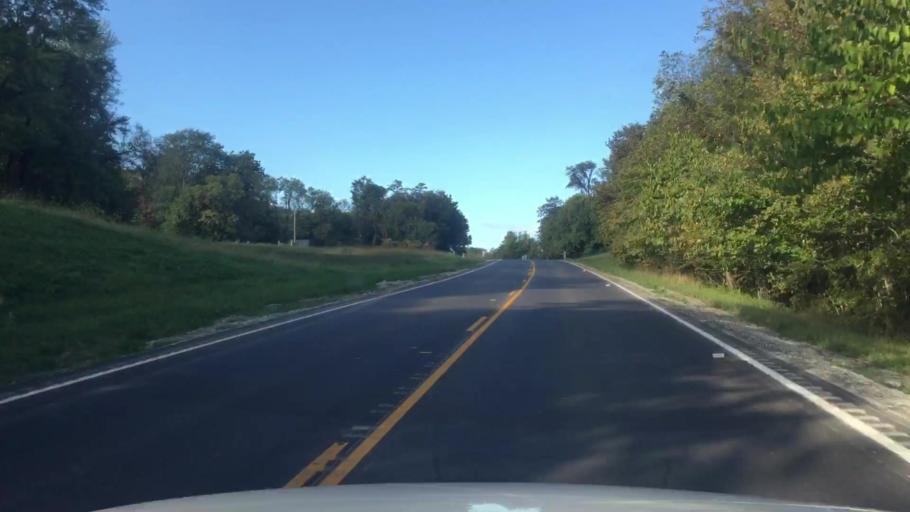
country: US
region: Missouri
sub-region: Howard County
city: New Franklin
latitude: 38.9972
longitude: -92.5983
